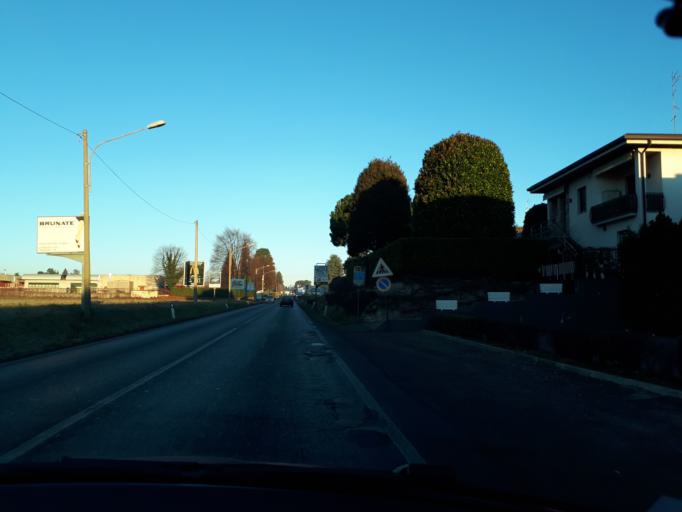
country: IT
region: Lombardy
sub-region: Provincia di Como
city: Vertemate Con Minoprio
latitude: 45.7280
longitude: 9.0654
